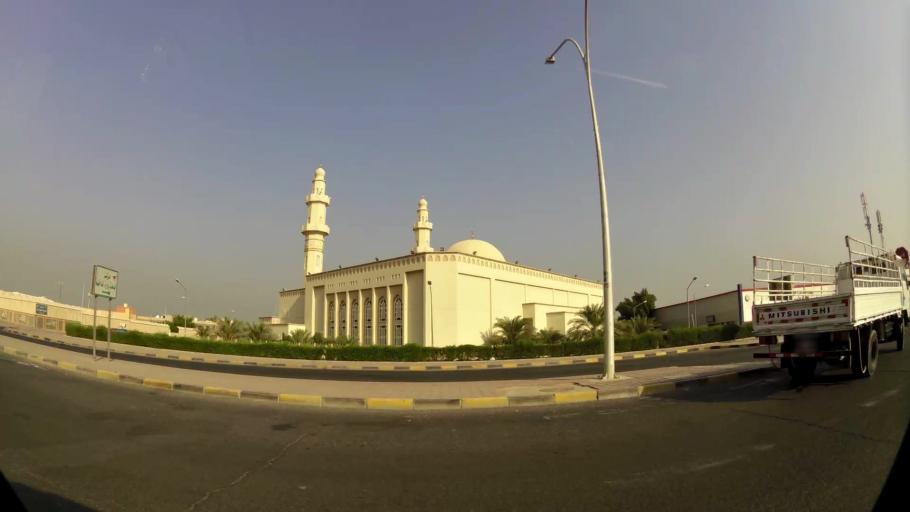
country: KW
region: Al Ahmadi
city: Al Manqaf
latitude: 29.1077
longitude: 48.1056
